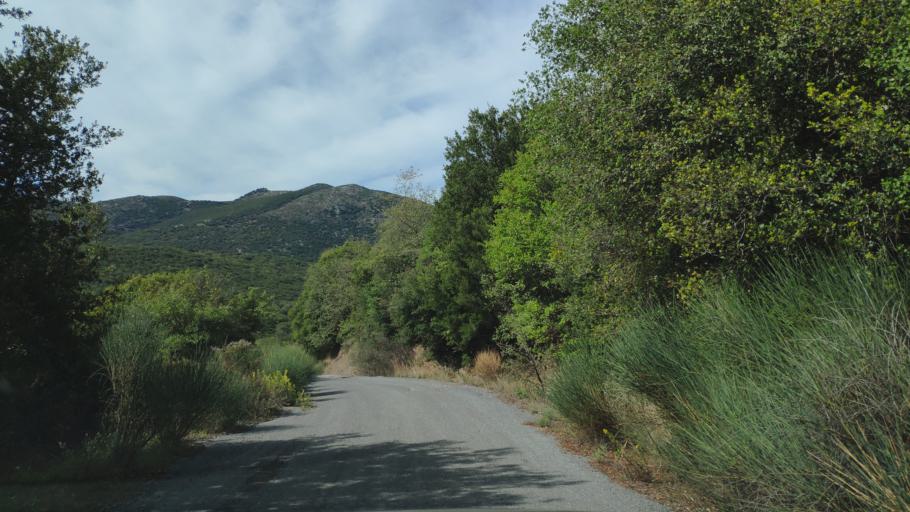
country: GR
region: Peloponnese
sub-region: Nomos Arkadias
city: Dimitsana
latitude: 37.5372
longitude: 22.0518
